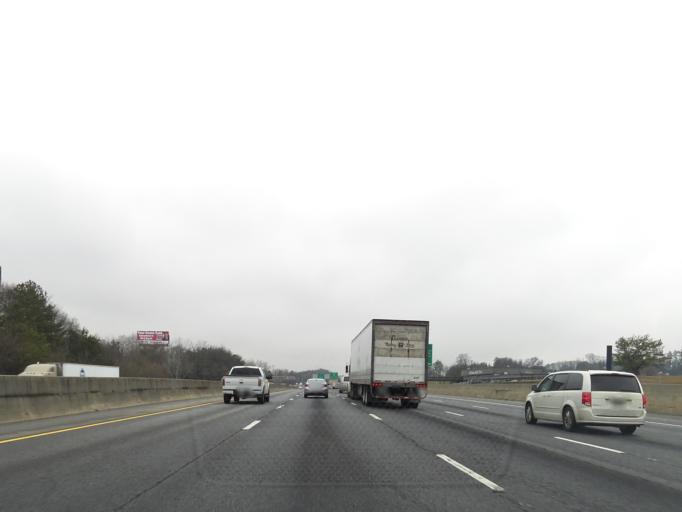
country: US
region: Georgia
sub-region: Clayton County
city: Forest Park
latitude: 33.6007
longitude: -84.3914
